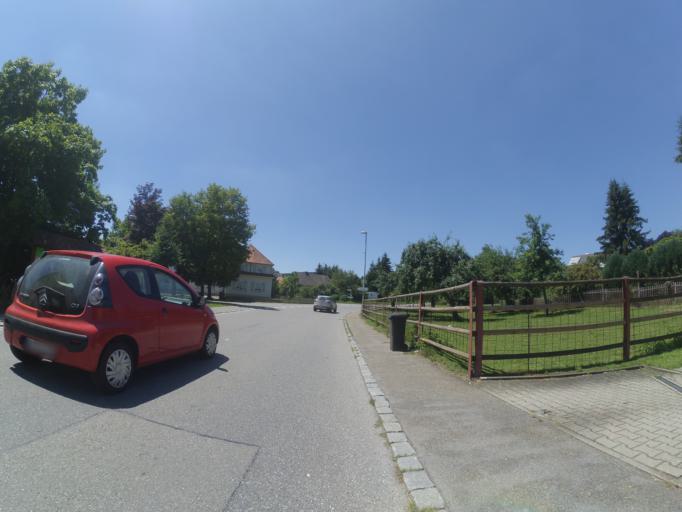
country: DE
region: Baden-Wuerttemberg
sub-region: Tuebingen Region
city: Bad Wurzach
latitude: 47.9049
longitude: 9.8303
